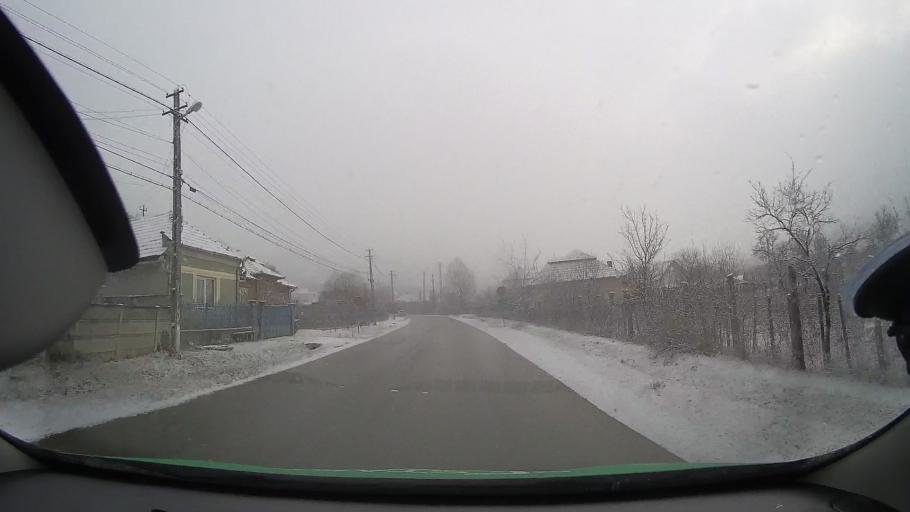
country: RO
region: Alba
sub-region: Municipiul Aiud
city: Ciumbrud
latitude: 46.3111
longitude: 23.7890
